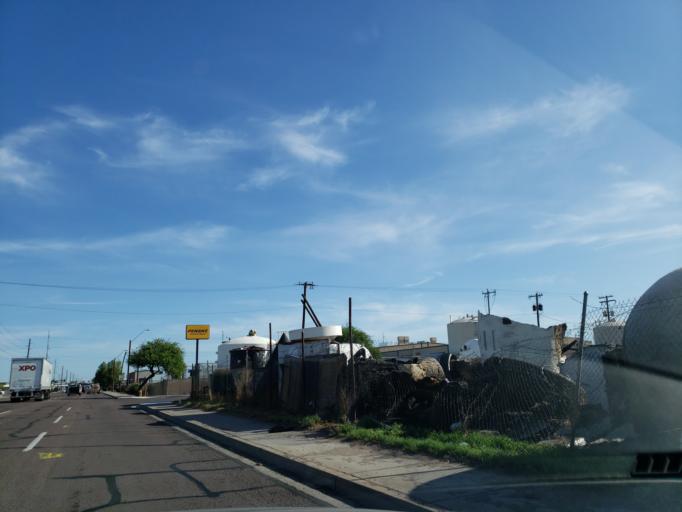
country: US
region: Arizona
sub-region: Maricopa County
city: Phoenix
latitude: 33.4701
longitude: -112.1170
